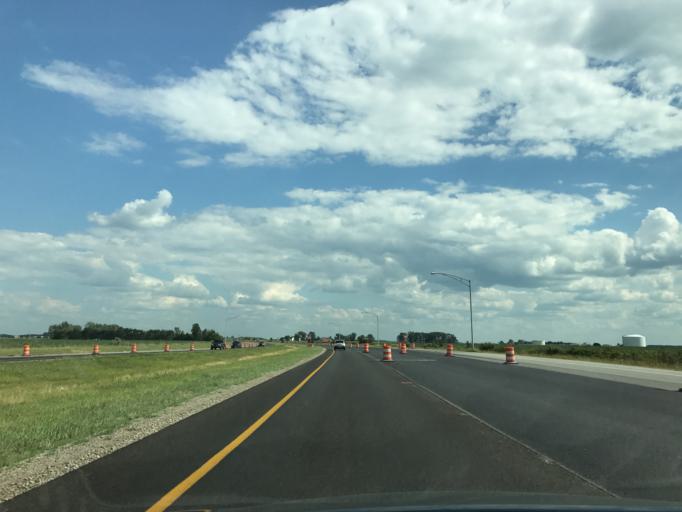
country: US
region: Ohio
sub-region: Van Wert County
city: Van Wert
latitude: 40.8768
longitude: -84.5227
